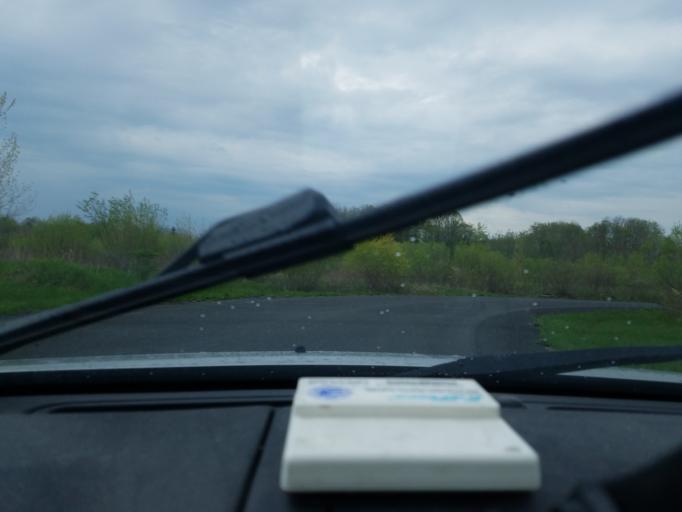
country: US
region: New York
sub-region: Onondaga County
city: East Syracuse
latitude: 43.1069
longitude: -76.0849
